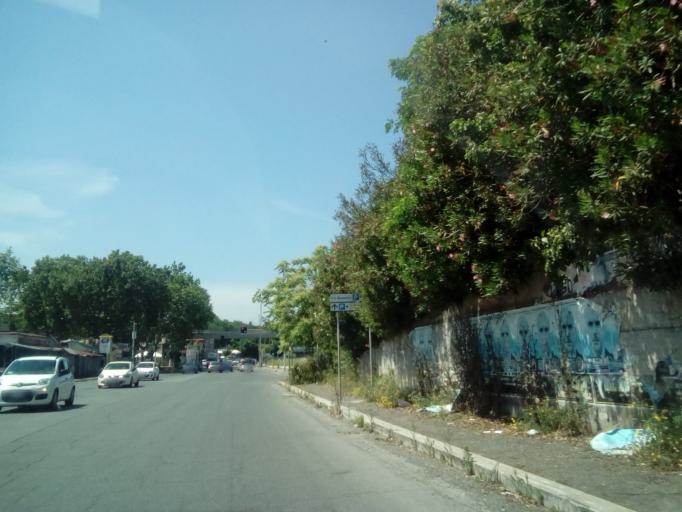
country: IT
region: Latium
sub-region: Citta metropolitana di Roma Capitale
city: Rome
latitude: 41.9163
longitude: 12.5623
